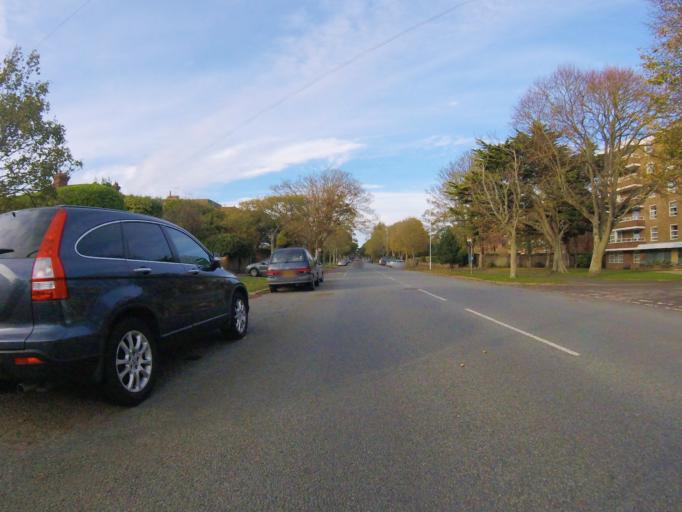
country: GB
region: England
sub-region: West Sussex
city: Worthing
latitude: 50.8110
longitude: -0.3930
